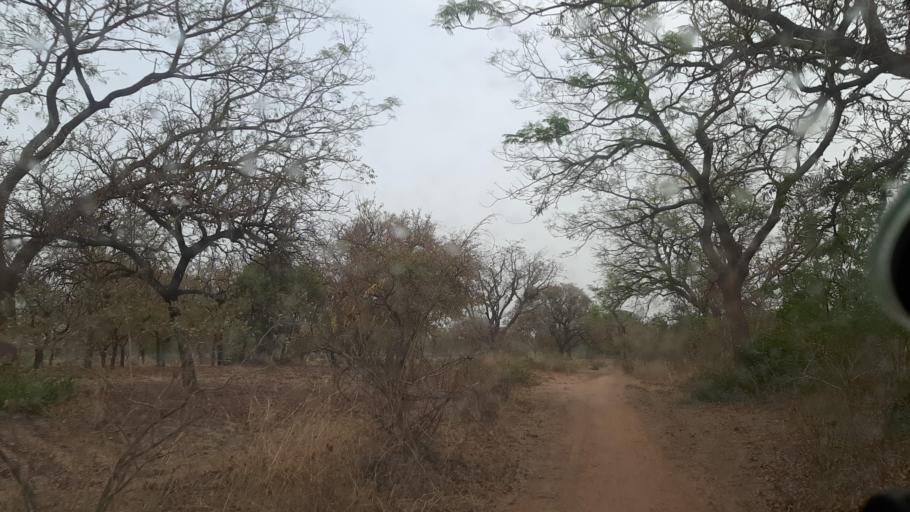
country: BF
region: Boucle du Mouhoun
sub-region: Province des Banwa
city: Salanso
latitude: 11.8596
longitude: -4.4344
